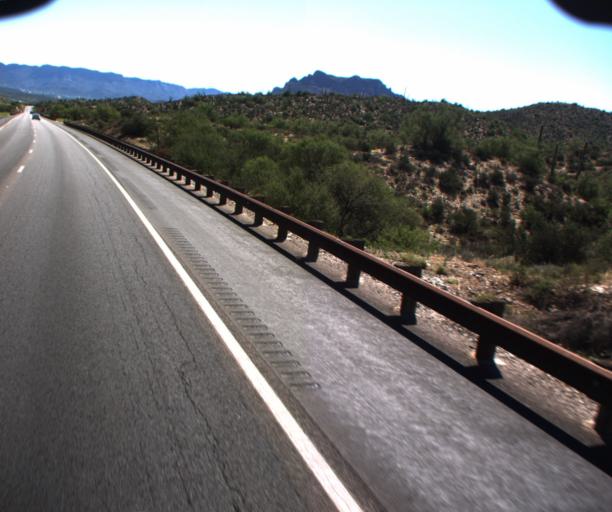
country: US
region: Arizona
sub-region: Pinal County
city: Gold Camp
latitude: 33.2725
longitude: -111.2152
